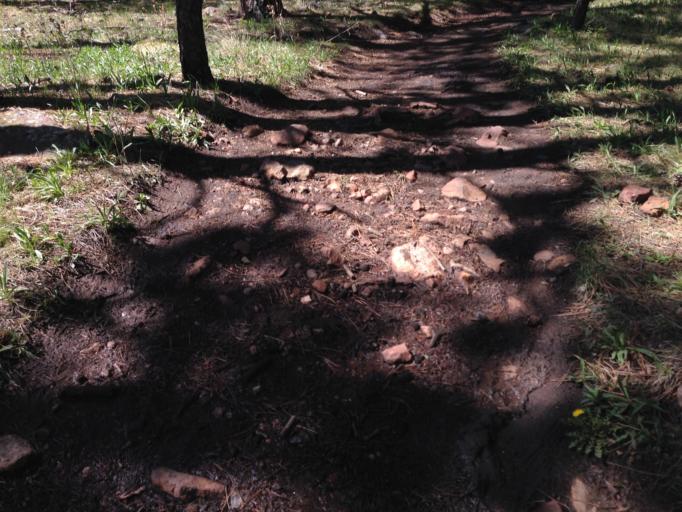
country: US
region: Colorado
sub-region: Boulder County
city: Boulder
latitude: 39.9179
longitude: -105.2691
